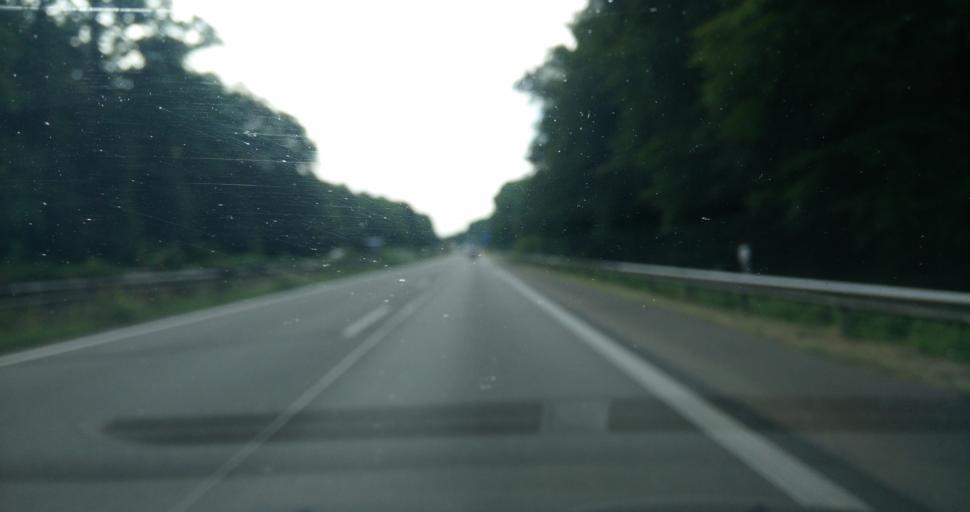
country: DE
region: Rheinland-Pfalz
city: Worth am Rhein
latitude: 49.0454
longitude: 8.2490
